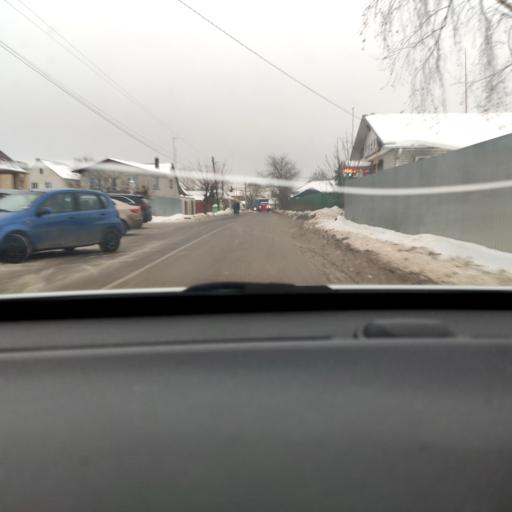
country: RU
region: Voronezj
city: Somovo
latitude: 51.7466
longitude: 39.3394
